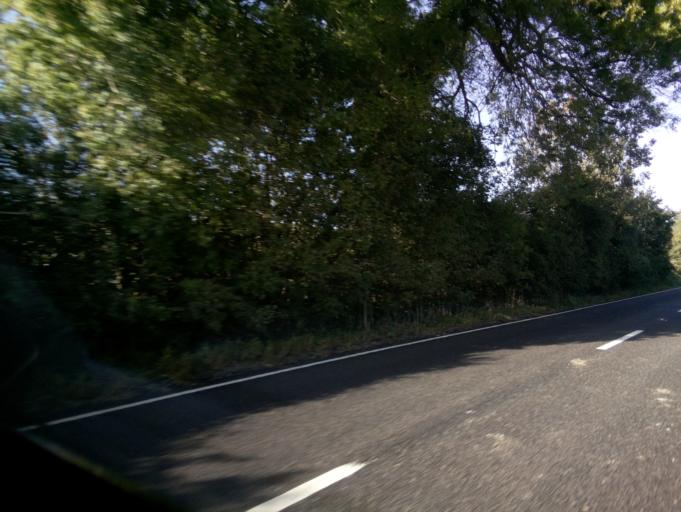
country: GB
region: England
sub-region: Hampshire
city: Four Marks
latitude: 51.0189
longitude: -1.0819
